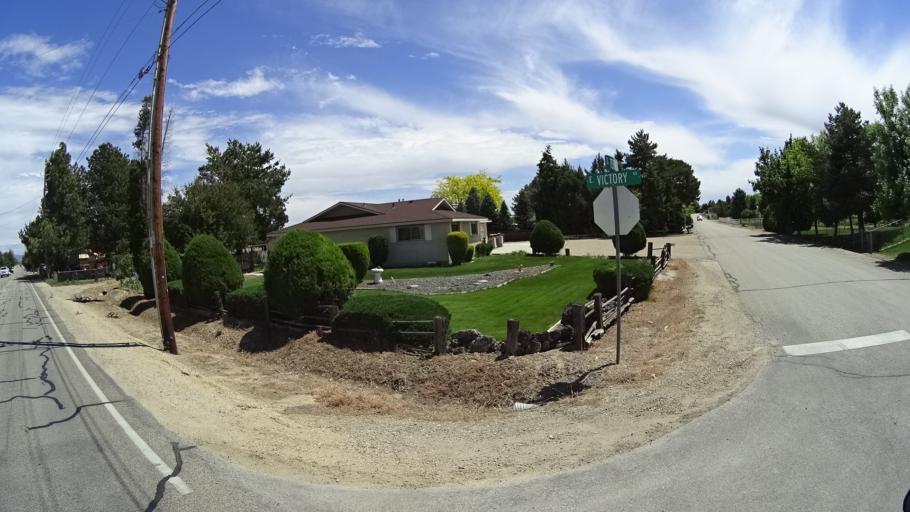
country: US
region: Idaho
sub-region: Ada County
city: Meridian
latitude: 43.5757
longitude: -116.3464
